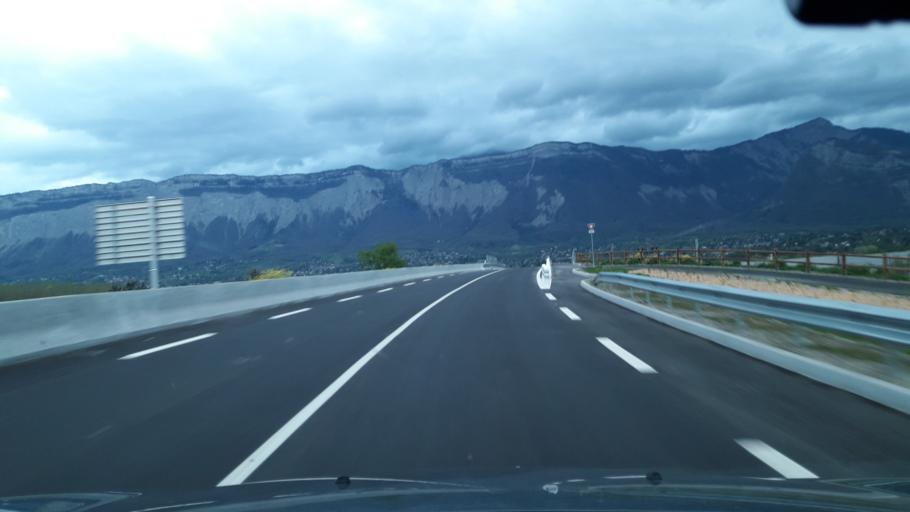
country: FR
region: Rhone-Alpes
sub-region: Departement de l'Isere
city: Le Versoud
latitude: 45.2270
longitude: 5.8718
